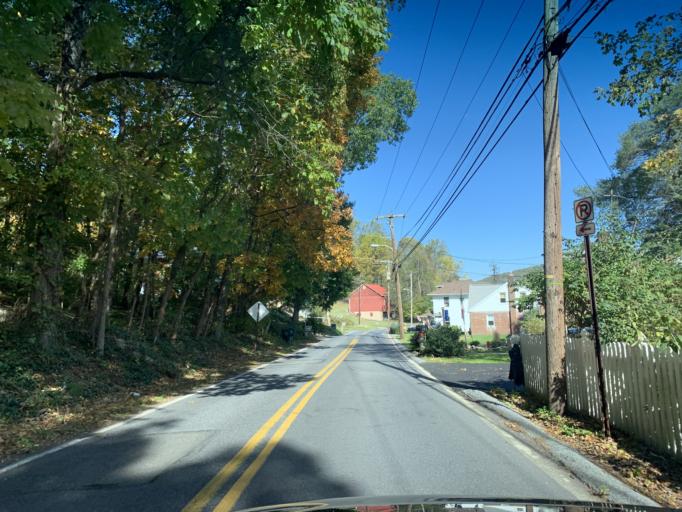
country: US
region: Pennsylvania
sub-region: Berks County
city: Reiffton
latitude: 40.3184
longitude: -75.8802
